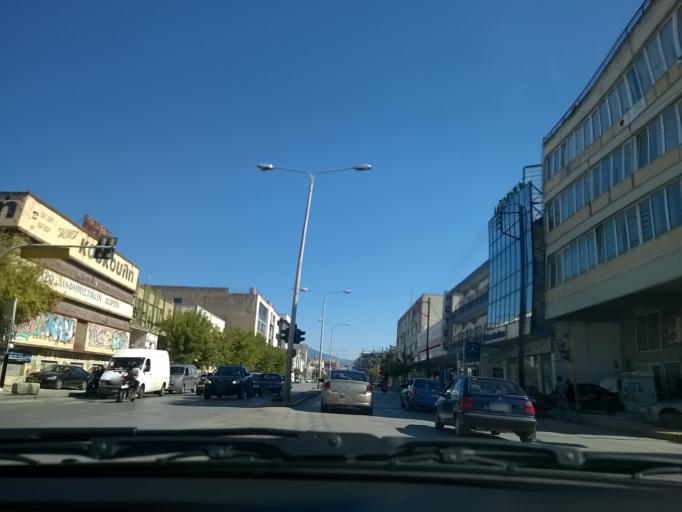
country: GR
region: Central Macedonia
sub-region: Nomos Thessalonikis
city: Menemeni
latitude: 40.6532
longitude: 22.9099
